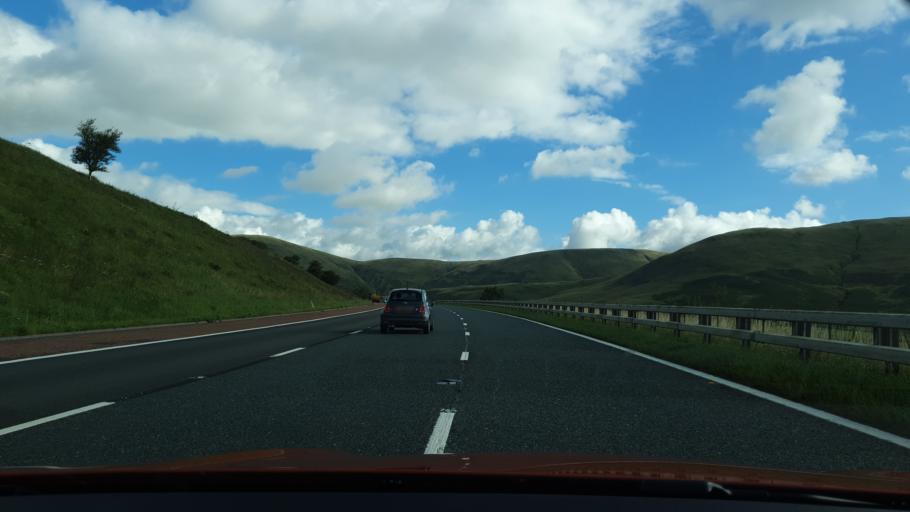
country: GB
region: England
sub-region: Cumbria
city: Sedbergh
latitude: 54.3699
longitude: -2.5852
